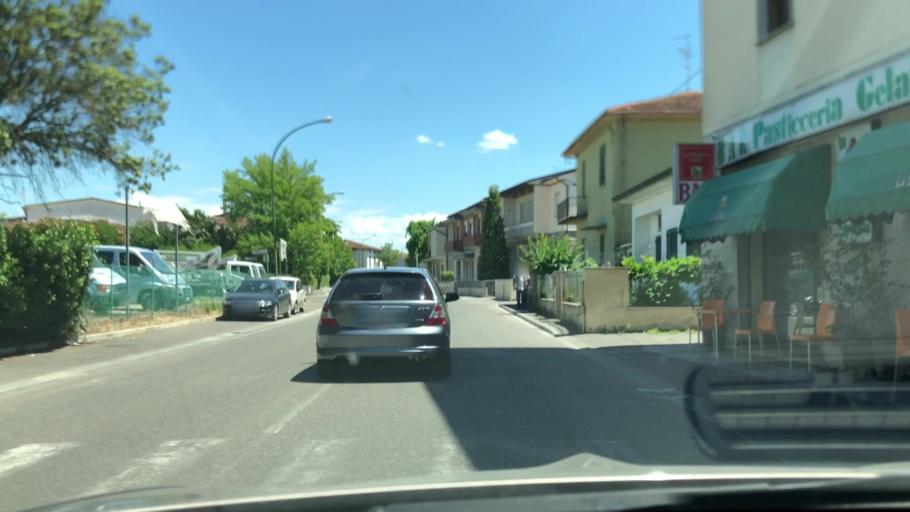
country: IT
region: Tuscany
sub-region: Province of Pisa
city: Ponsacco
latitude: 43.6182
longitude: 10.6364
